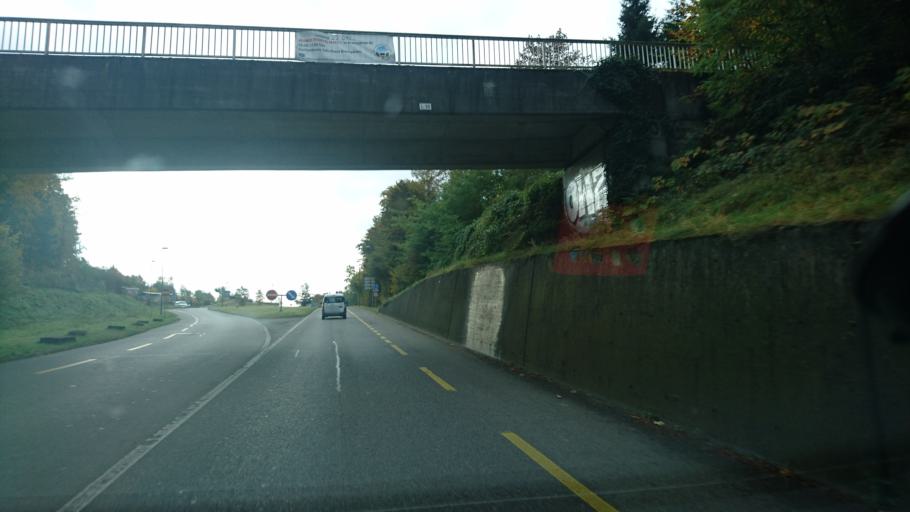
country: CH
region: Bern
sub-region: Bern-Mittelland District
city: Bern
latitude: 46.9682
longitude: 7.4282
